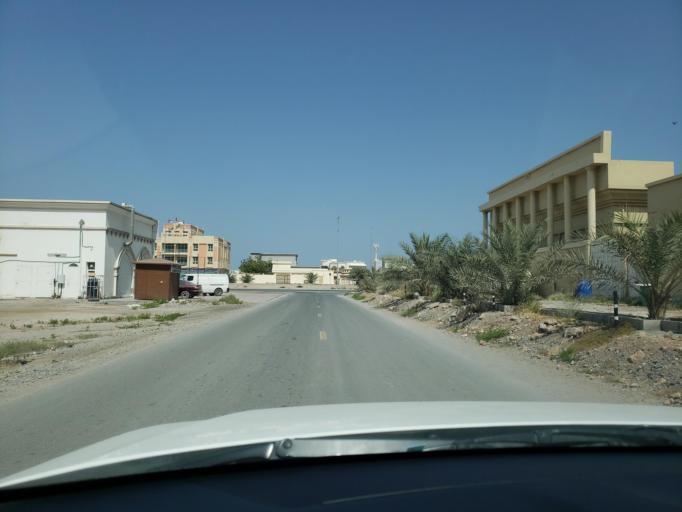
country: AE
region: Ra's al Khaymah
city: Ras al-Khaimah
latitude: 25.8577
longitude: 56.0158
